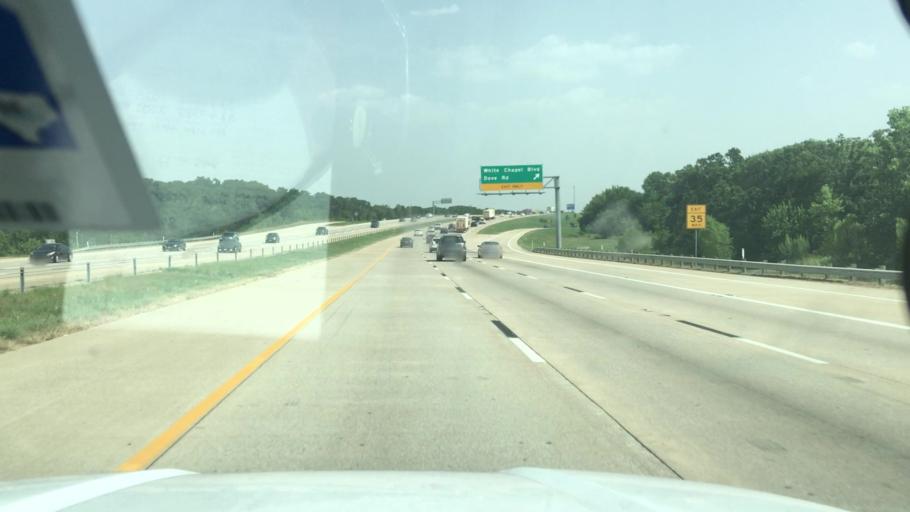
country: US
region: Texas
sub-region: Denton County
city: Trophy Club
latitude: 32.9755
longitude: -97.1618
